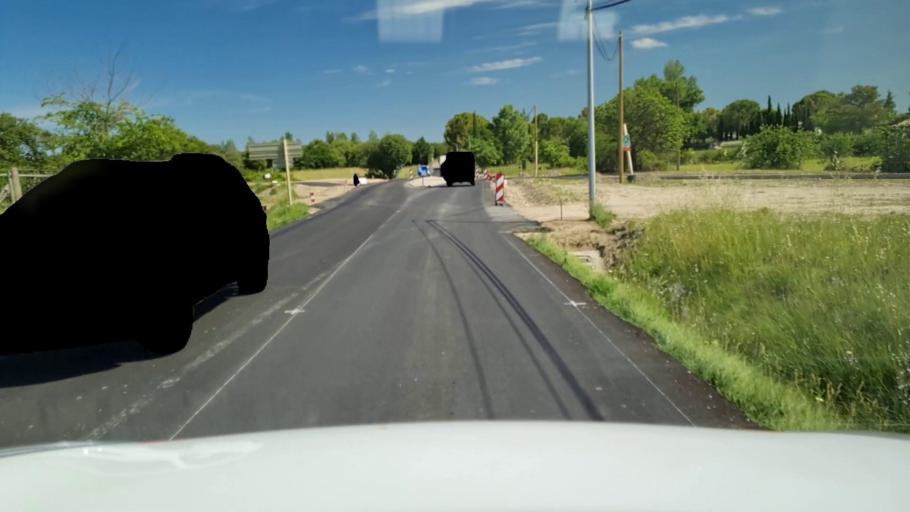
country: FR
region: Languedoc-Roussillon
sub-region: Departement du Gard
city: Sommieres
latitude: 43.7965
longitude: 4.0860
